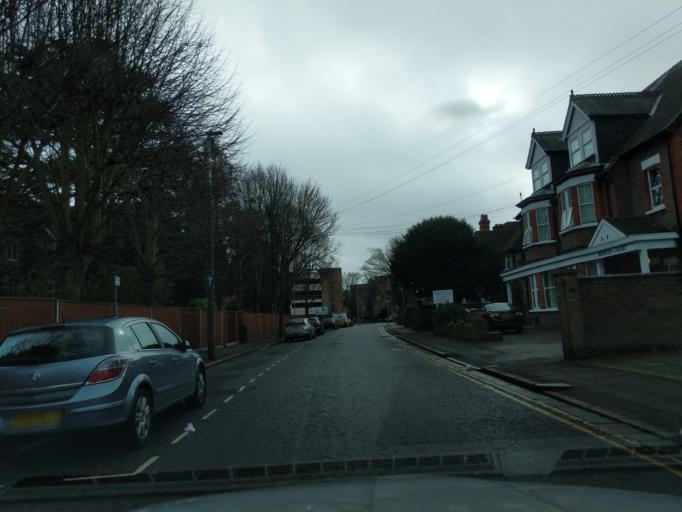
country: GB
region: England
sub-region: Hertfordshire
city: Watford
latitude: 51.6583
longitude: -0.4026
